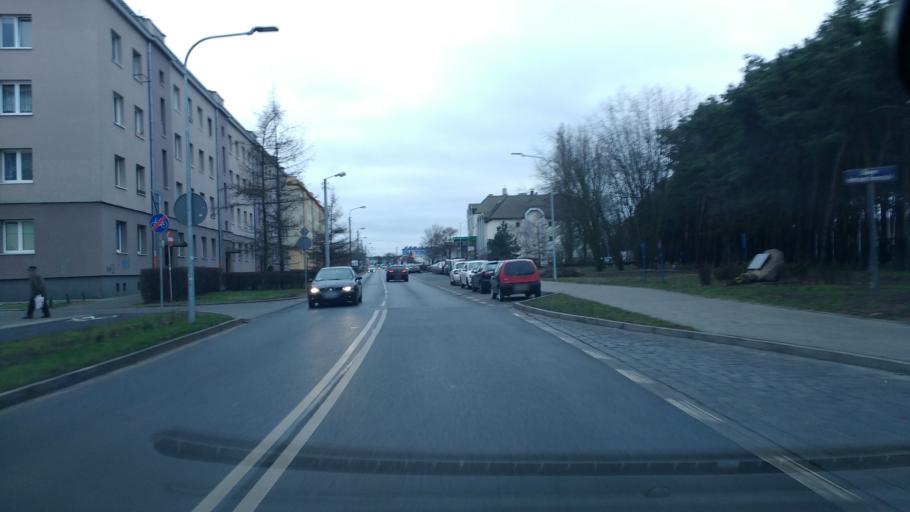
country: PL
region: Kujawsko-Pomorskie
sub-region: Bydgoszcz
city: Bydgoszcz
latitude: 53.1434
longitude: 18.0311
